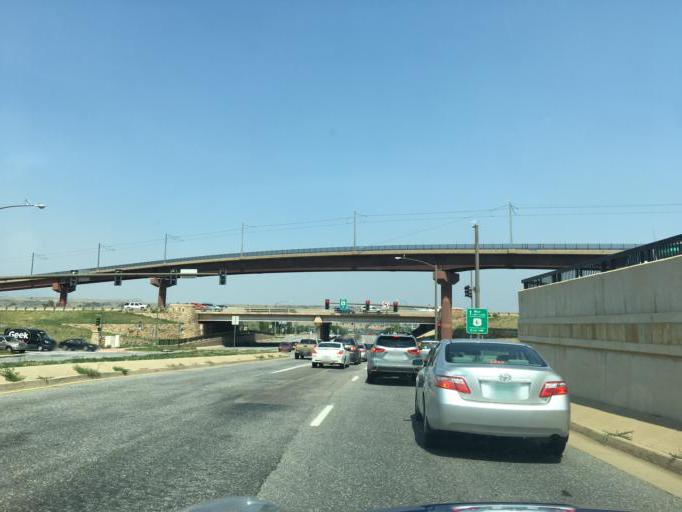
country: US
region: Colorado
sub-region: Jefferson County
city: West Pleasant View
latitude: 39.7241
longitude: -105.1654
